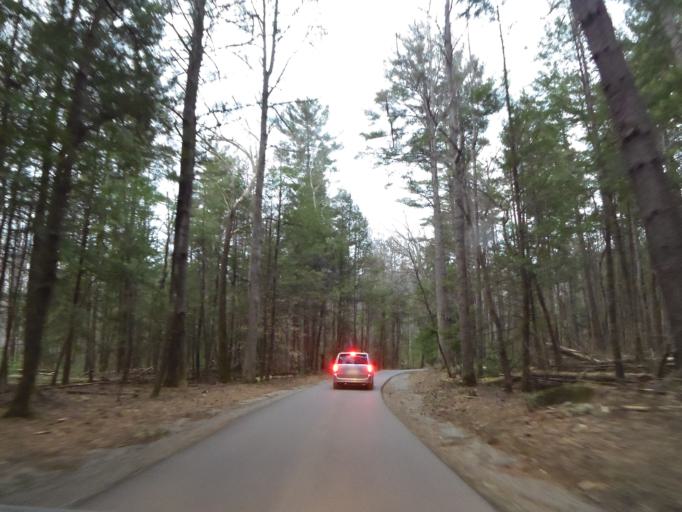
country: US
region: Tennessee
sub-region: Blount County
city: Wildwood
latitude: 35.5966
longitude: -83.7877
